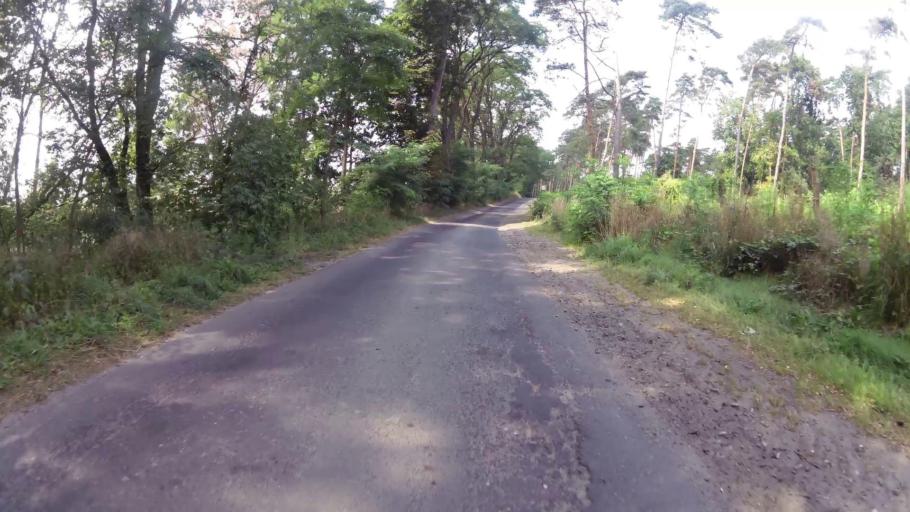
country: PL
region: West Pomeranian Voivodeship
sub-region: Powiat gryfinski
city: Mieszkowice
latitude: 52.8709
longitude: 14.5205
